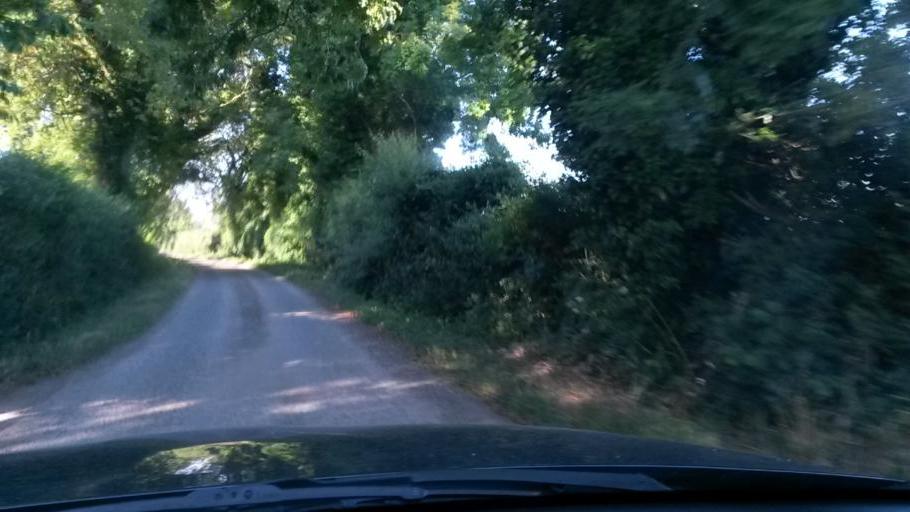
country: IE
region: Leinster
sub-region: Dublin City
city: Finglas
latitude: 53.4457
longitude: -6.3118
